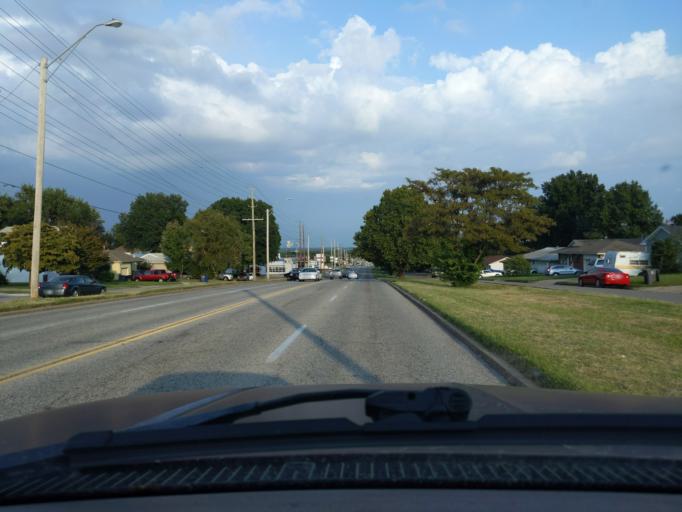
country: US
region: Oklahoma
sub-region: Tulsa County
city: Tulsa
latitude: 36.1334
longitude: -95.9106
